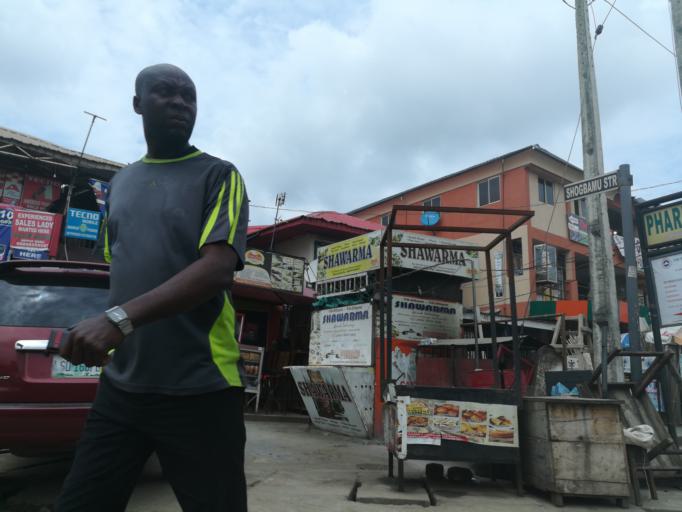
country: NG
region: Lagos
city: Somolu
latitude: 6.5474
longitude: 3.3946
